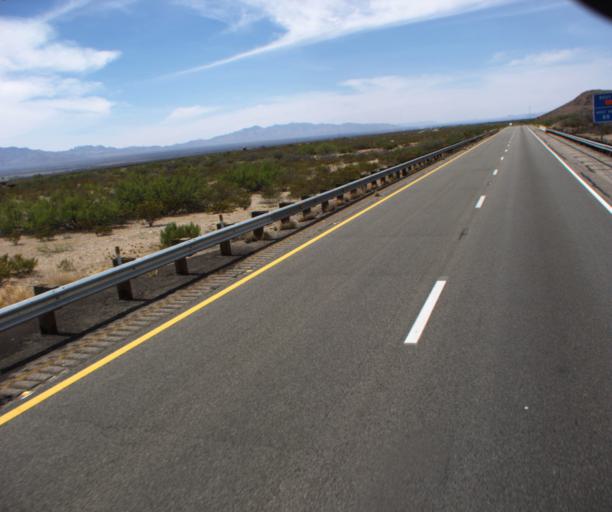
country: US
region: New Mexico
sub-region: Hidalgo County
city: Lordsburg
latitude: 32.2354
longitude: -109.0753
